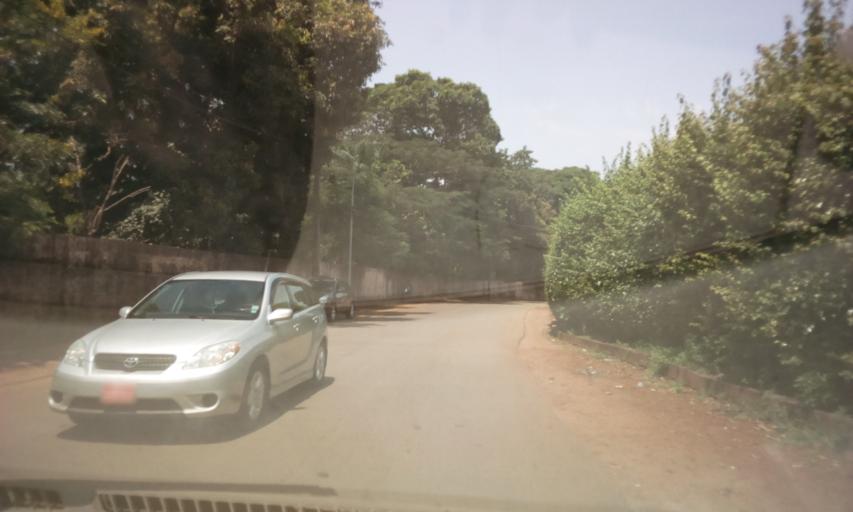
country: GN
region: Conakry
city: Conakry
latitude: 9.5687
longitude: -13.6652
